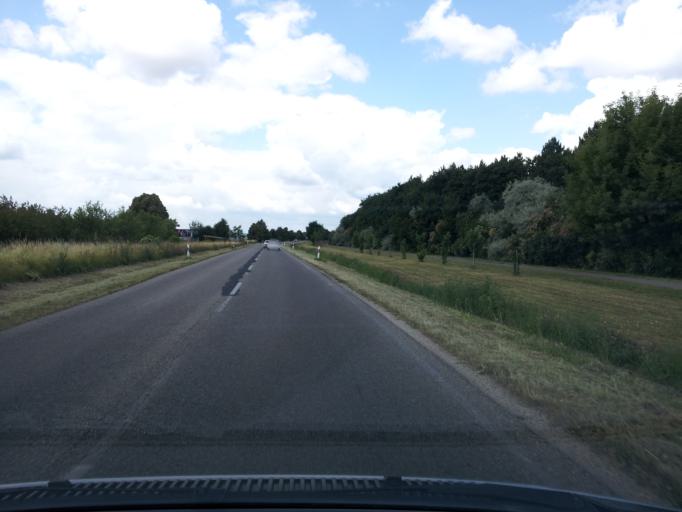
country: HU
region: Veszprem
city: Szentkiralyszabadja
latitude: 47.0722
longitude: 17.9421
